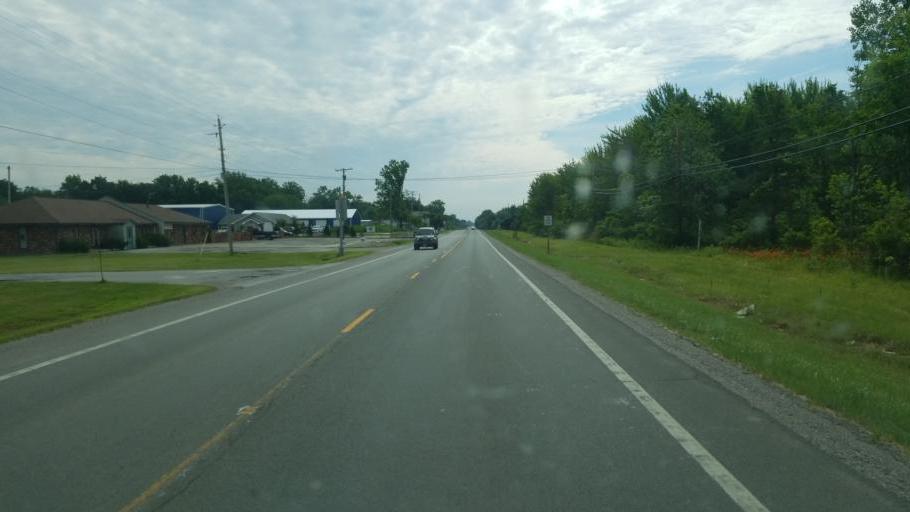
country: US
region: Ohio
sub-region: Lorain County
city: Eaton Estates
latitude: 41.3142
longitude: -82.0145
